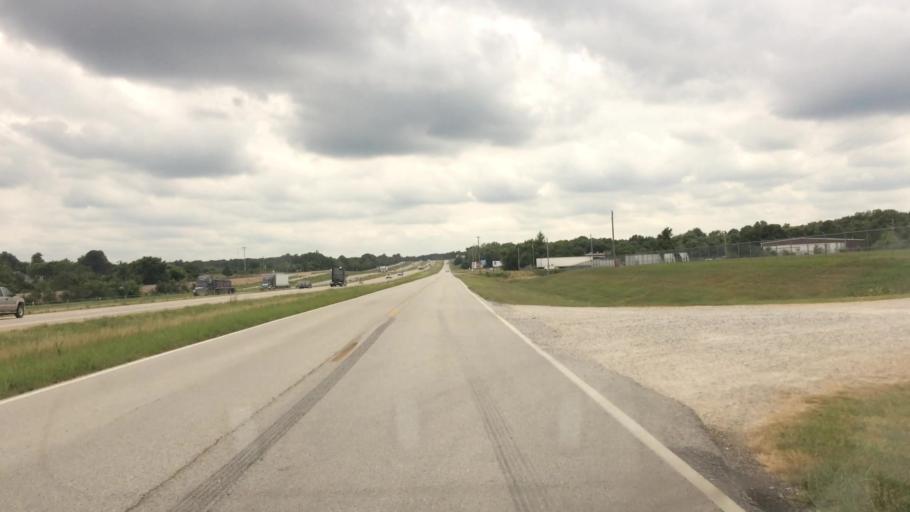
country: US
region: Missouri
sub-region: Greene County
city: Strafford
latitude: 37.2925
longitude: -93.0266
